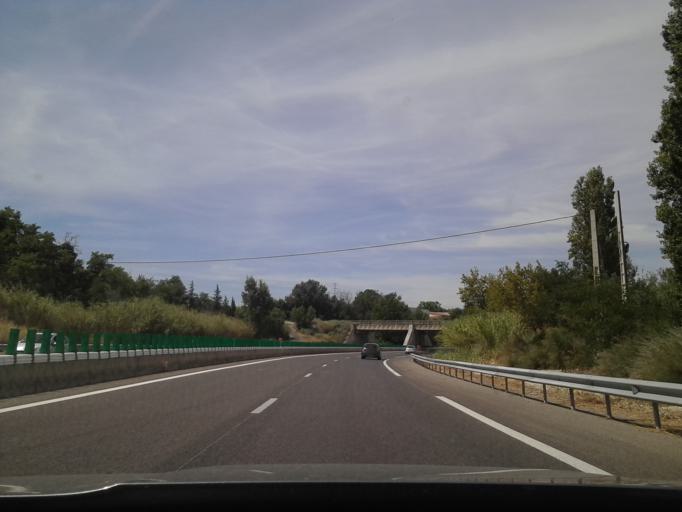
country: FR
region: Languedoc-Roussillon
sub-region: Departement des Pyrenees-Orientales
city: Baho
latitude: 42.6921
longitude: 2.8347
